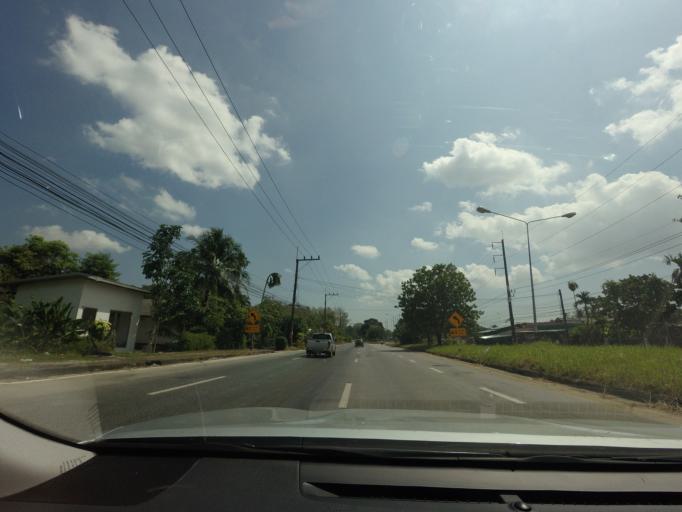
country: TH
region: Phangnga
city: Thai Mueang
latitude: 8.2721
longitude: 98.3270
